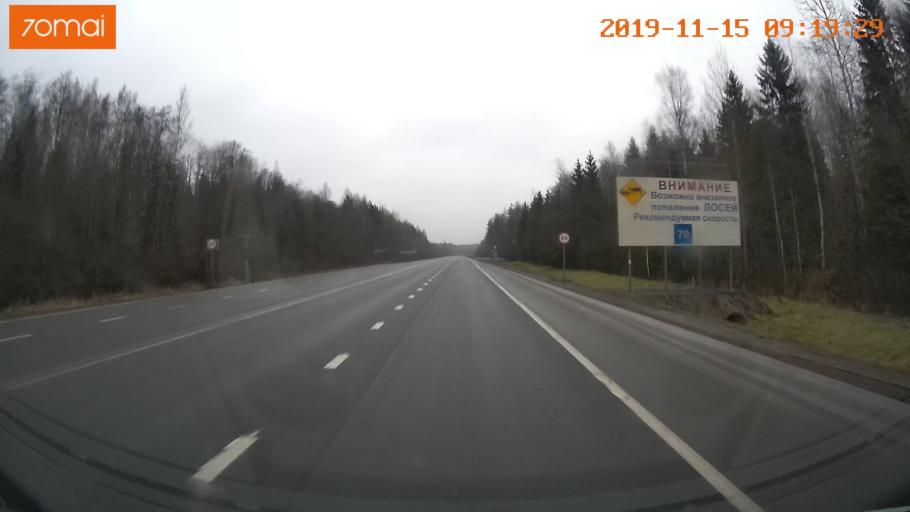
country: RU
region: Vologda
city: Tonshalovo
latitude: 59.2841
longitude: 38.0169
